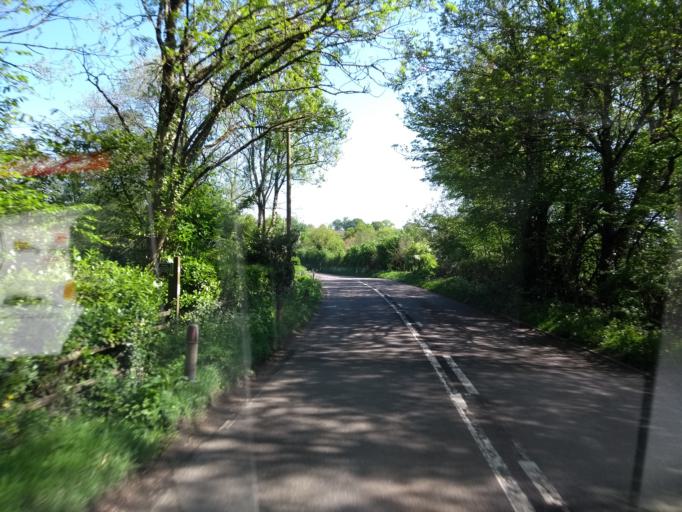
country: GB
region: England
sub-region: Devon
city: Axminster
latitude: 50.8160
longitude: -2.9729
